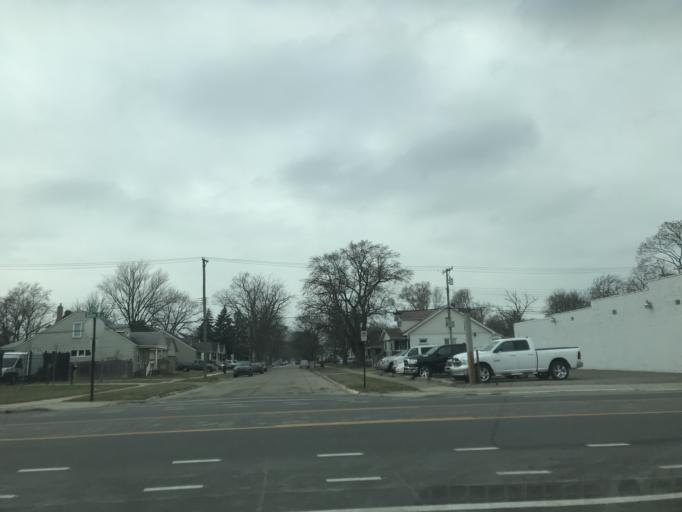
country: US
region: Michigan
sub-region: Oakland County
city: Hazel Park
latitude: 42.4501
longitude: -83.1029
